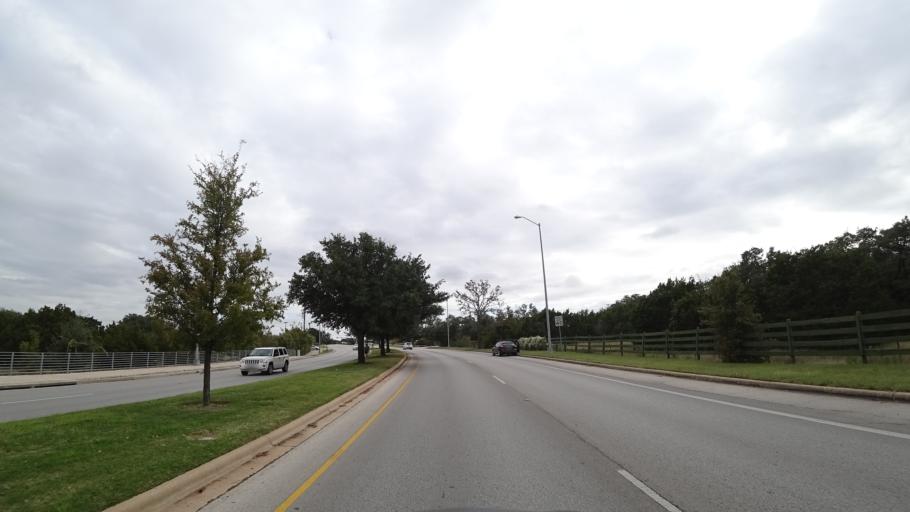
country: US
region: Texas
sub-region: Williamson County
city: Brushy Creek
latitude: 30.5093
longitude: -97.7176
